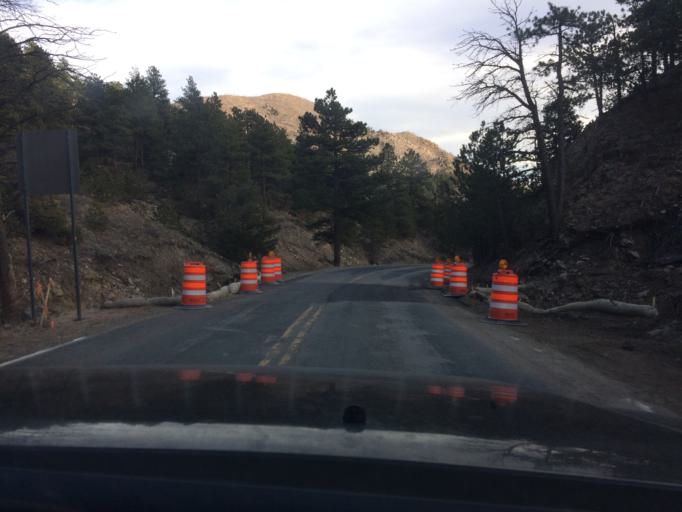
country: US
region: Colorado
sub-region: Boulder County
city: Lyons
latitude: 40.1307
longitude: -105.4054
